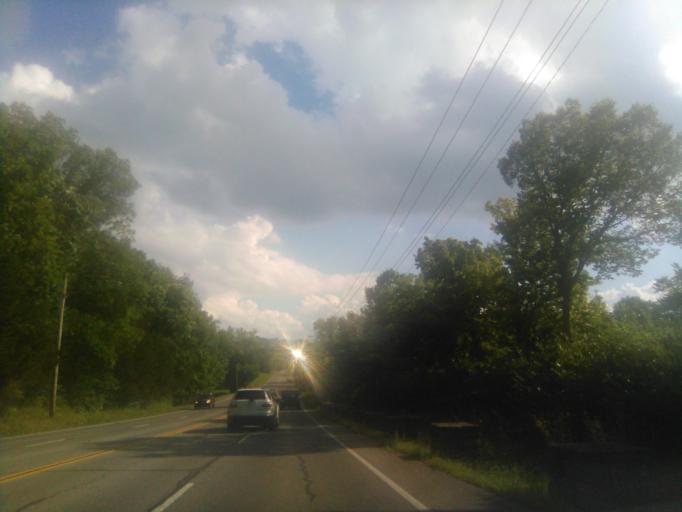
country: US
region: Tennessee
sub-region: Davidson County
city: Belle Meade
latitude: 36.0847
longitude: -86.8827
